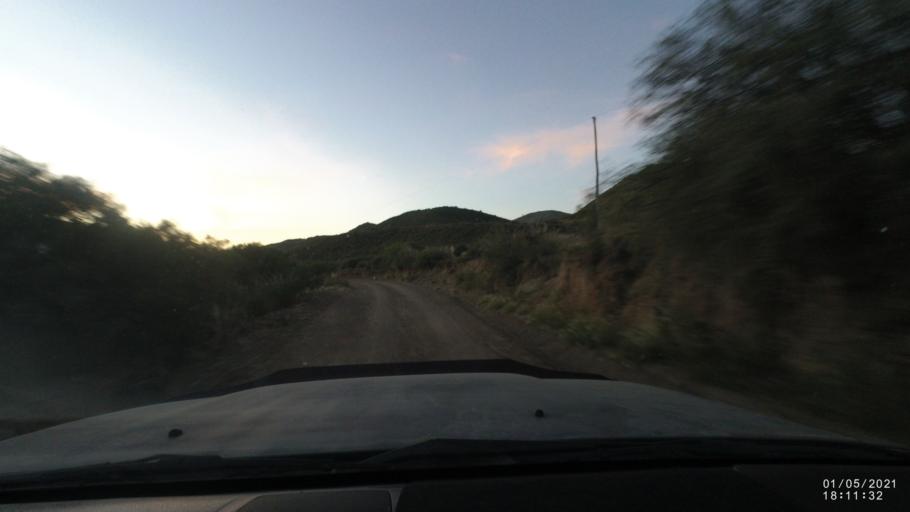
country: BO
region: Cochabamba
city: Capinota
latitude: -17.6821
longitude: -66.1997
